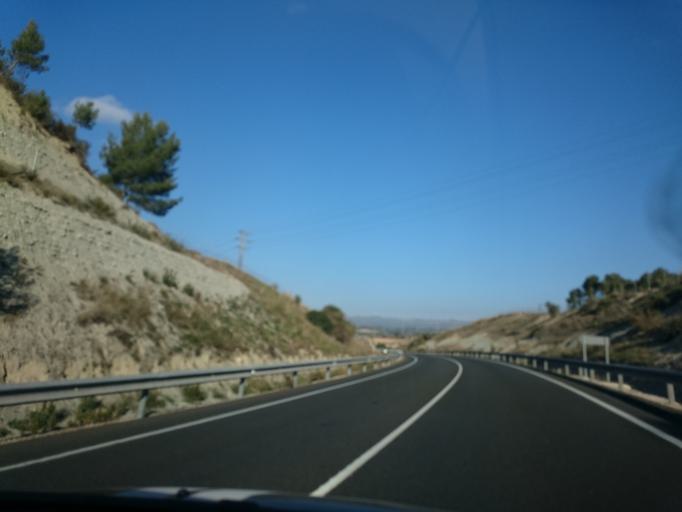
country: ES
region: Catalonia
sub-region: Provincia de Barcelona
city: La Pobla de Claramunt
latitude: 41.5737
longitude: 1.6734
